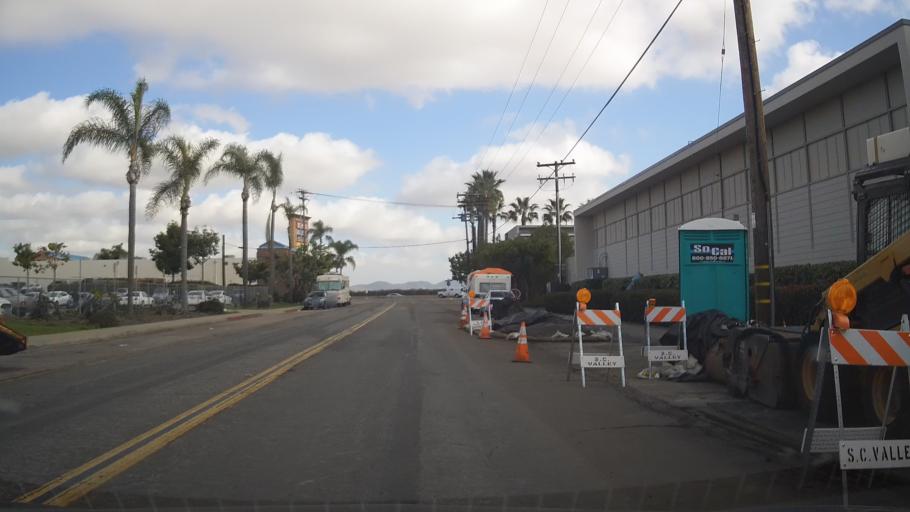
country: US
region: California
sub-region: San Diego County
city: San Diego
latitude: 32.8172
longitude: -117.1513
